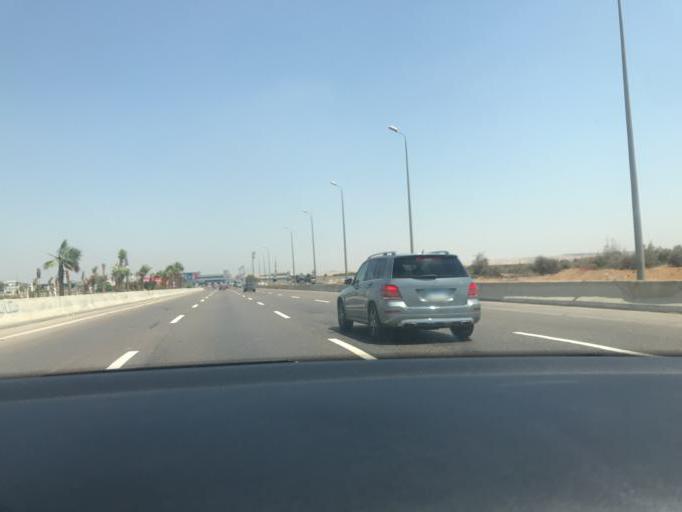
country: EG
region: Al Jizah
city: Awsim
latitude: 30.0732
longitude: 31.0077
